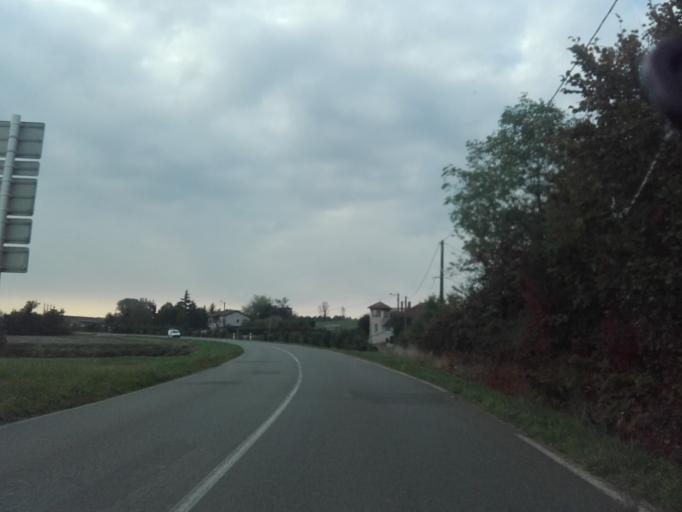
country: FR
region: Bourgogne
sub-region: Departement de Saone-et-Loire
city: Charnay-les-Macon
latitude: 46.2950
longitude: 4.7682
